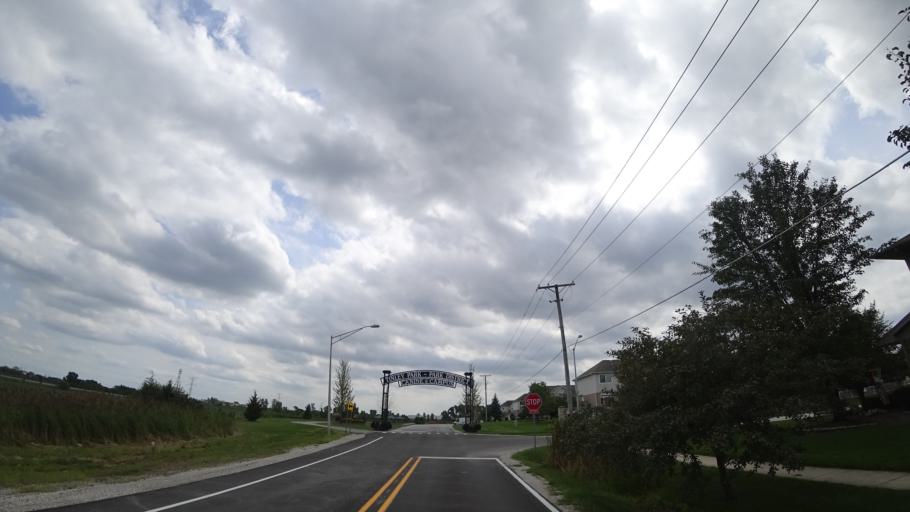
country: US
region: Illinois
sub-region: Cook County
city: Orland Hills
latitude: 41.5624
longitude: -87.8222
